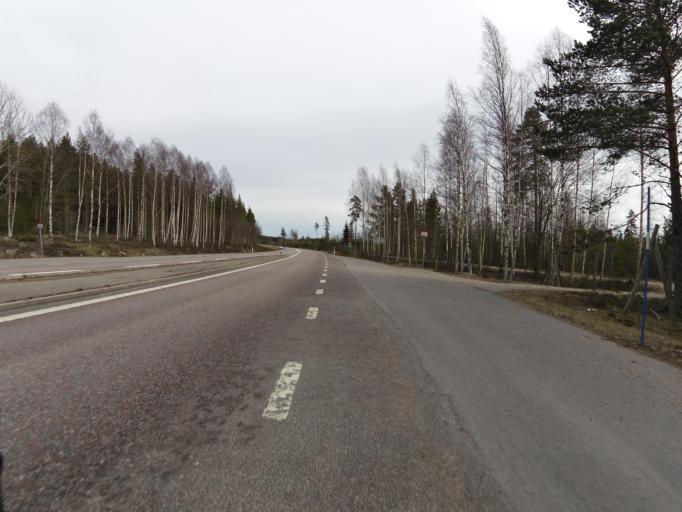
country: SE
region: Gaevleborg
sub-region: Hofors Kommun
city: Hofors
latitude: 60.5424
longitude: 16.2312
